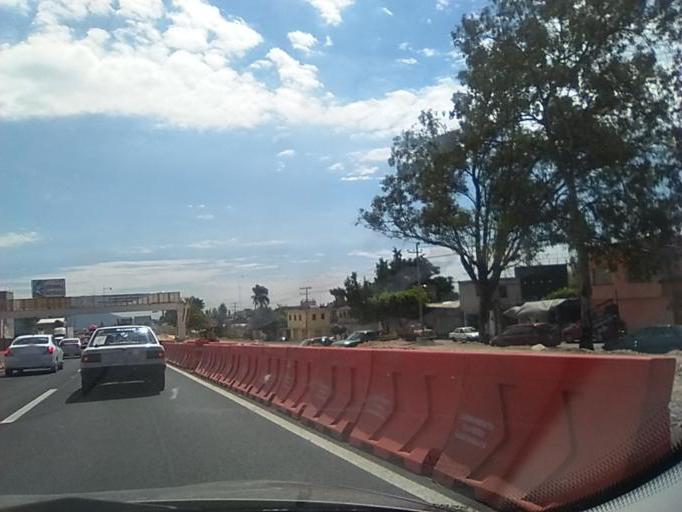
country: MX
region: Morelos
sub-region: Cuernavaca
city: Colonia los Cerritos
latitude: 18.9558
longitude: -99.2005
